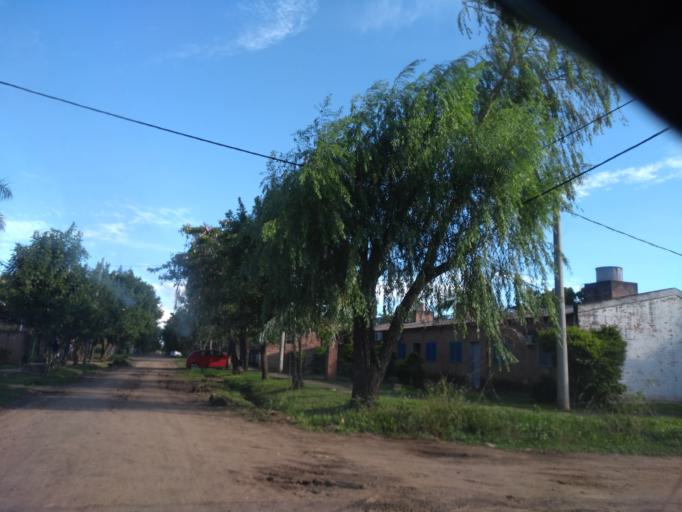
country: AR
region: Chaco
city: Fontana
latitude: -27.4110
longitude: -59.0400
